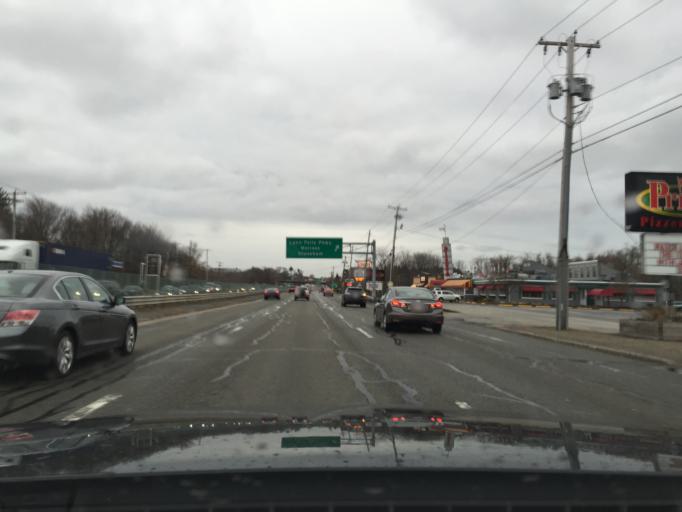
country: US
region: Massachusetts
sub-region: Essex County
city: Saugus
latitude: 42.4844
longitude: -71.0194
